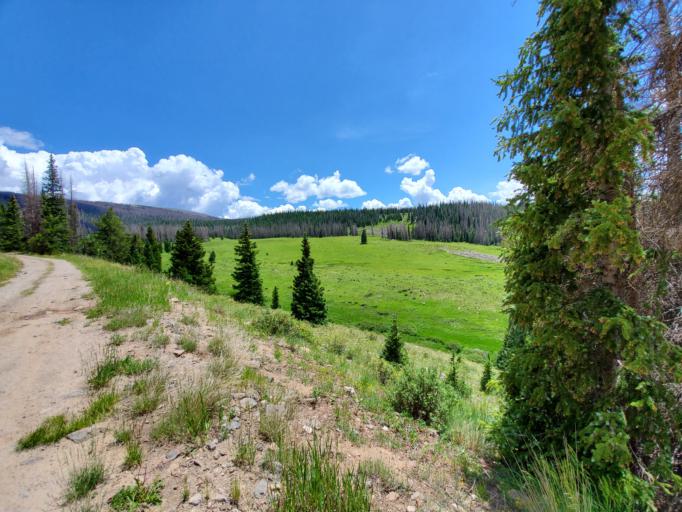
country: US
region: Colorado
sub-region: Rio Grande County
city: Del Norte
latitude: 37.5510
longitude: -106.5904
